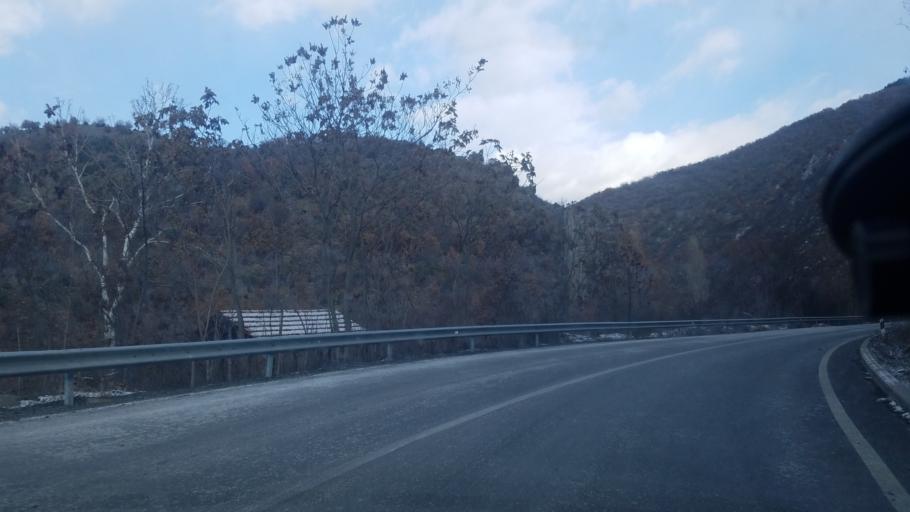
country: MK
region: Vinica
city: Vinica
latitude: 41.9437
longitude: 22.5320
